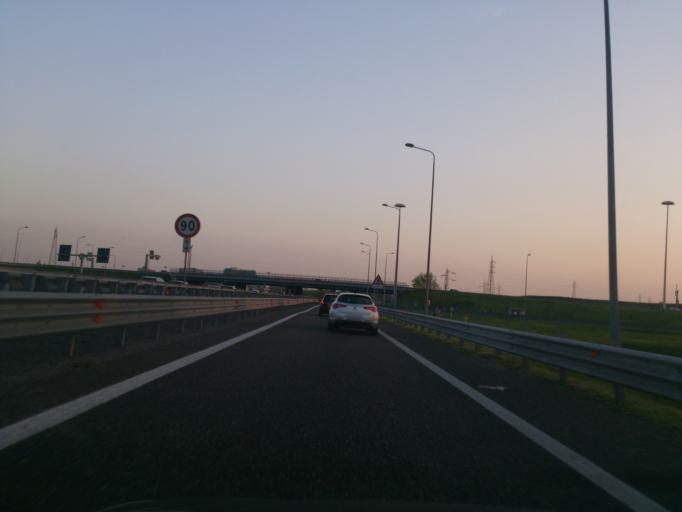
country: IT
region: Lombardy
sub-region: Citta metropolitana di Milano
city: Linate
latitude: 45.4378
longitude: 9.2560
